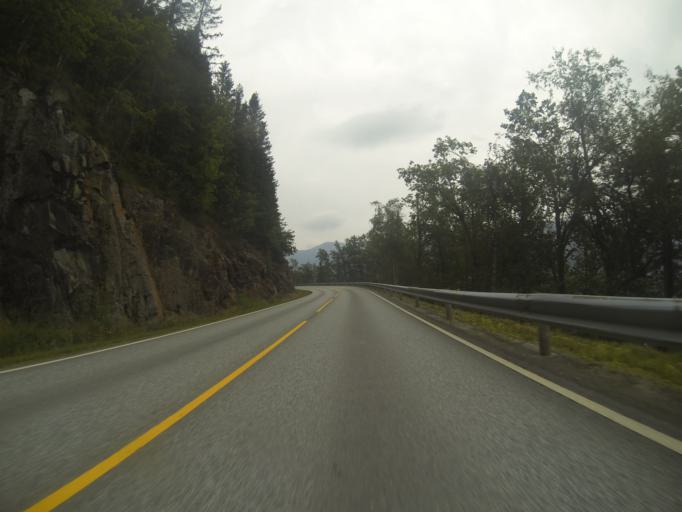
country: NO
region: Rogaland
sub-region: Suldal
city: Sand
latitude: 59.5577
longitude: 6.2626
